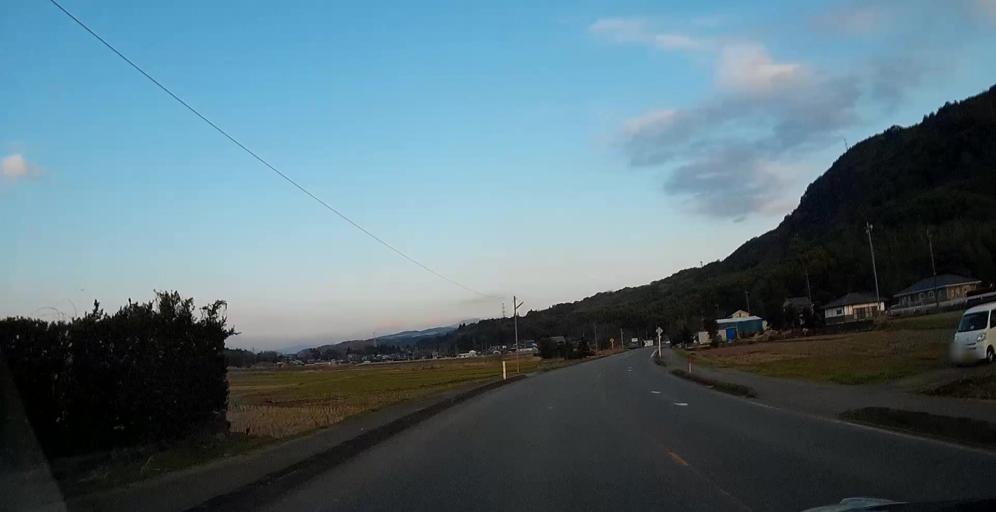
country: JP
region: Kumamoto
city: Ozu
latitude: 32.7692
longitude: 130.8187
